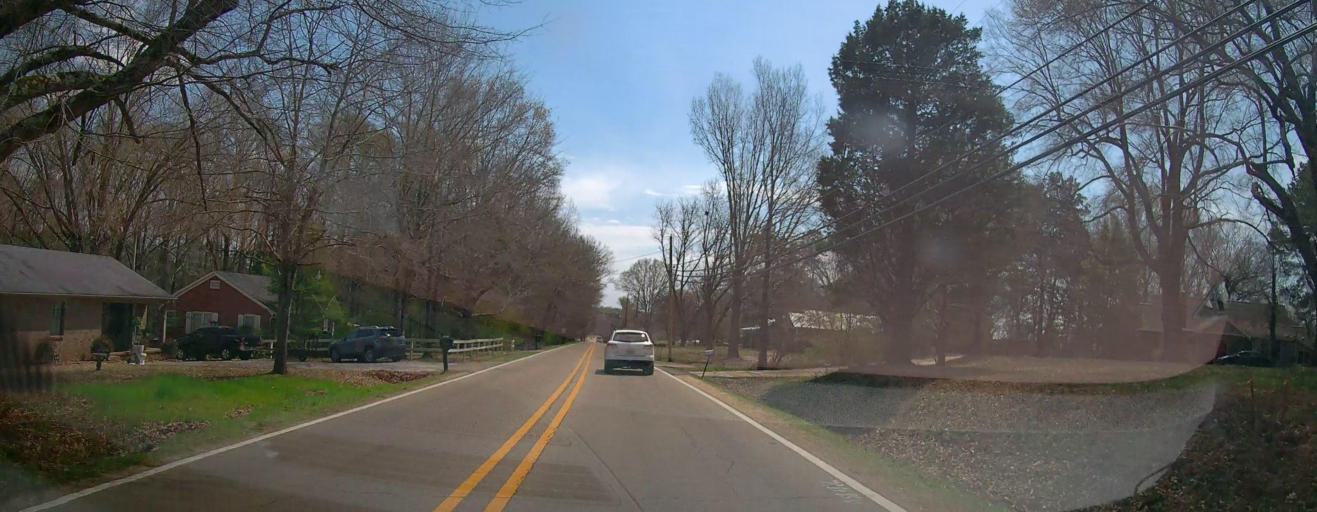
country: US
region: Mississippi
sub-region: Union County
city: New Albany
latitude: 34.4784
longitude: -88.9982
